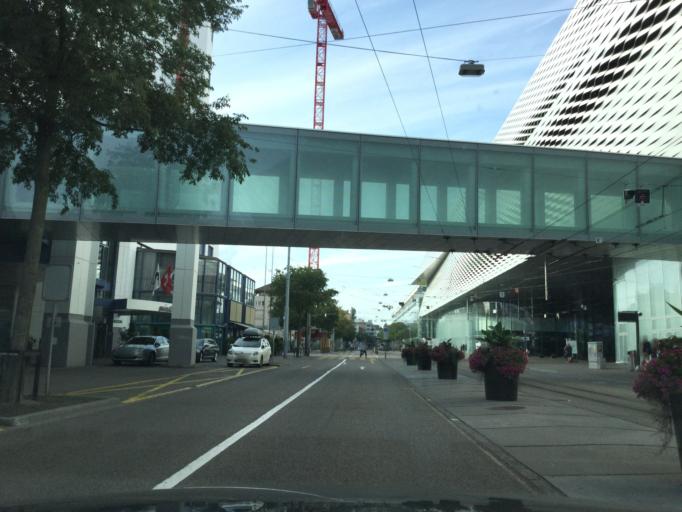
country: CH
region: Basel-Landschaft
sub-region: Bezirk Arlesheim
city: Birsfelden
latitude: 47.5627
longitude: 7.5998
